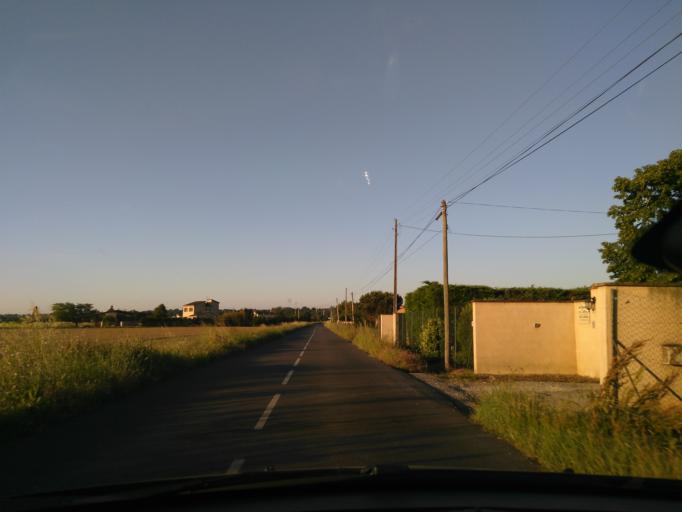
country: FR
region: Midi-Pyrenees
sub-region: Departement de la Haute-Garonne
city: Grenade
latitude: 43.7490
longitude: 1.2855
